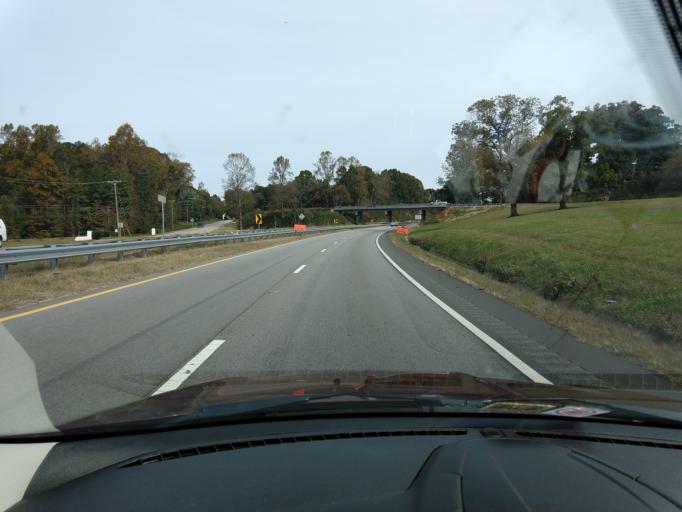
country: US
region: Virginia
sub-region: Pittsylvania County
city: Chatham
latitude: 36.8055
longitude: -79.3931
